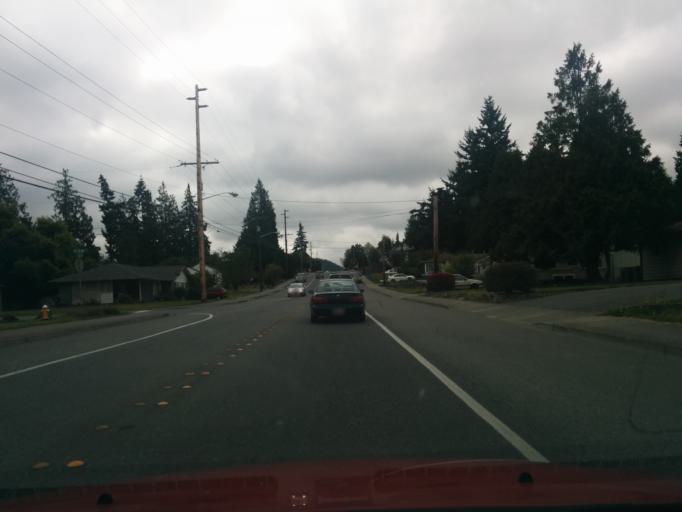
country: US
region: Washington
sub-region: Skagit County
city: Mount Vernon
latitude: 48.4273
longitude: -122.3135
